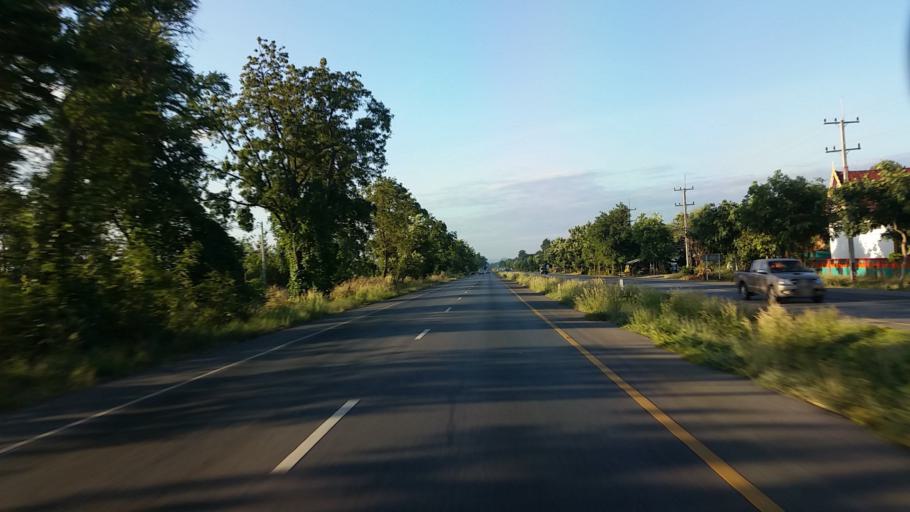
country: TH
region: Lop Buri
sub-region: Amphoe Tha Luang
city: Tha Luang
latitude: 15.1233
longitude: 101.0347
